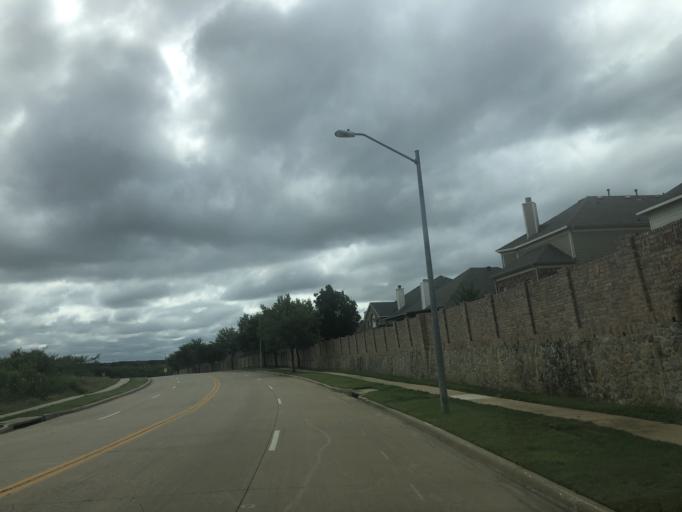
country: US
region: Texas
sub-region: Dallas County
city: Cedar Hill
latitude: 32.6576
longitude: -96.9990
